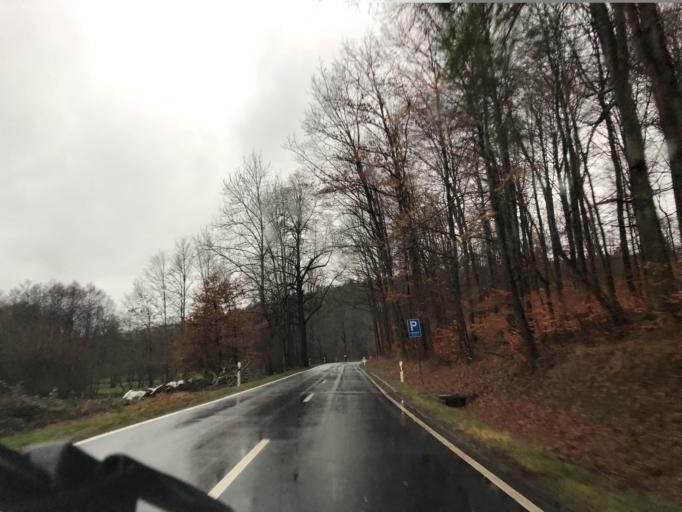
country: DE
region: Hesse
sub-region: Regierungsbezirk Darmstadt
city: Bad Konig
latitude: 49.7381
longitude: 9.0388
